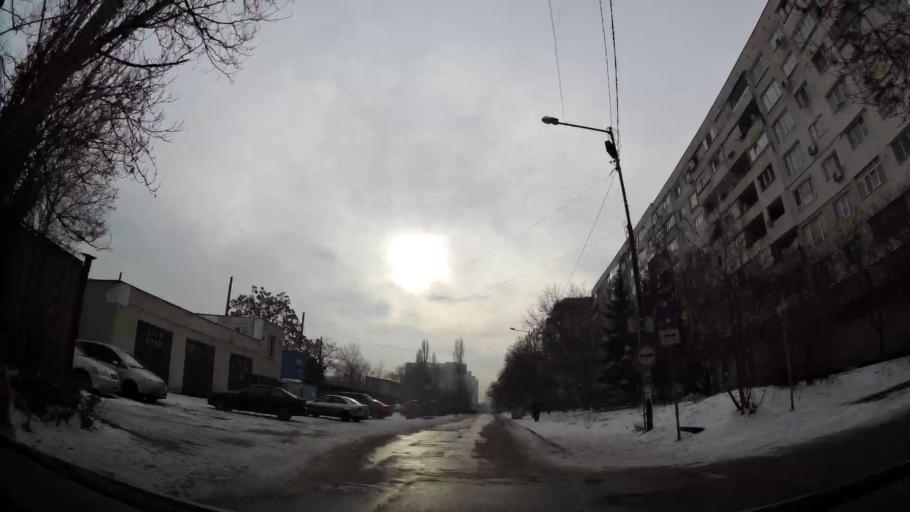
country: BG
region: Sofia-Capital
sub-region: Stolichna Obshtina
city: Sofia
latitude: 42.7159
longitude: 23.3057
